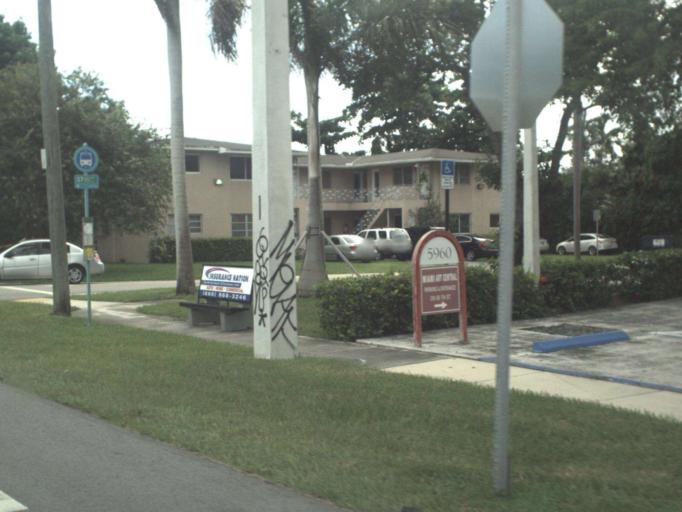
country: US
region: Florida
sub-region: Miami-Dade County
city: South Miami
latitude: 25.7156
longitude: -80.2858
